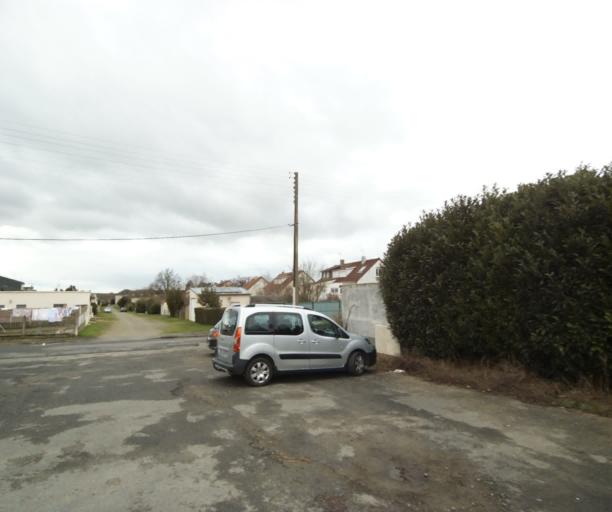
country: FR
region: Pays de la Loire
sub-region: Departement de la Sarthe
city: Le Mans
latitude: 47.9629
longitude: 0.2000
